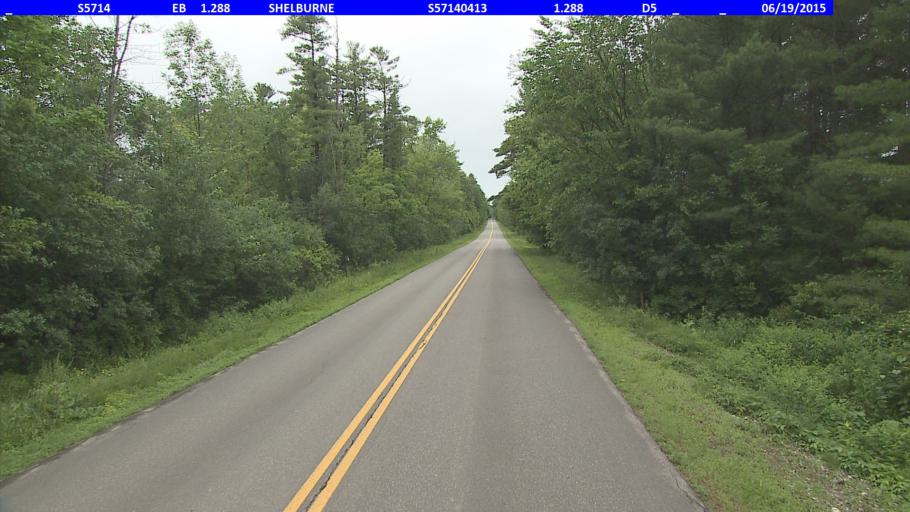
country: US
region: Vermont
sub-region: Chittenden County
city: Burlington
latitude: 44.3903
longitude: -73.2456
